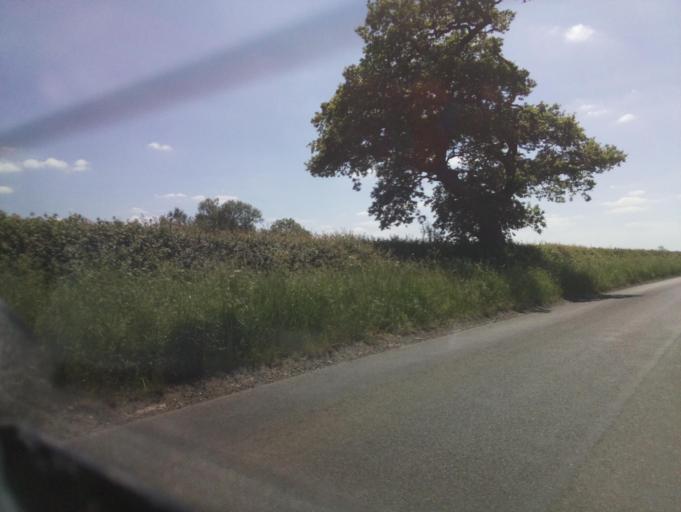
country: GB
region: England
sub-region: Wiltshire
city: Lyneham
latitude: 51.4888
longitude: -1.9362
